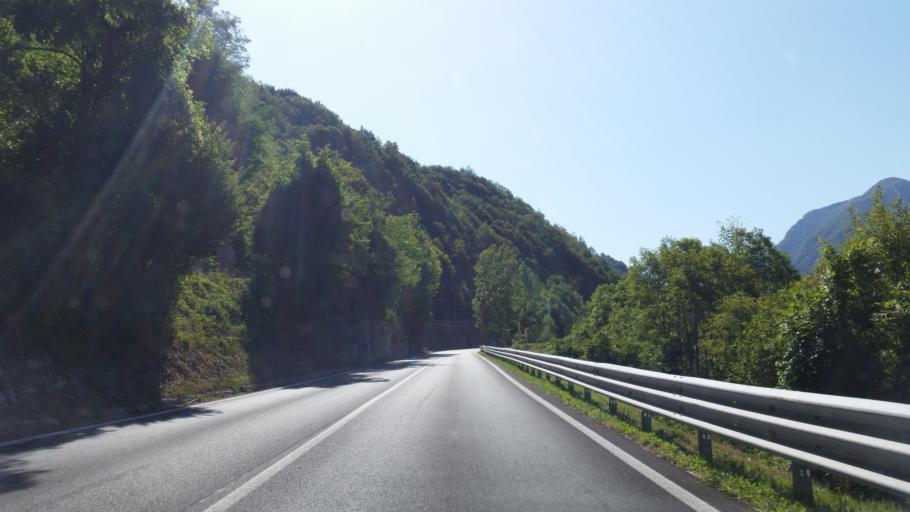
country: IT
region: Piedmont
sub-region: Provincia di Cuneo
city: Vernante
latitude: 44.2603
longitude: 7.5219
